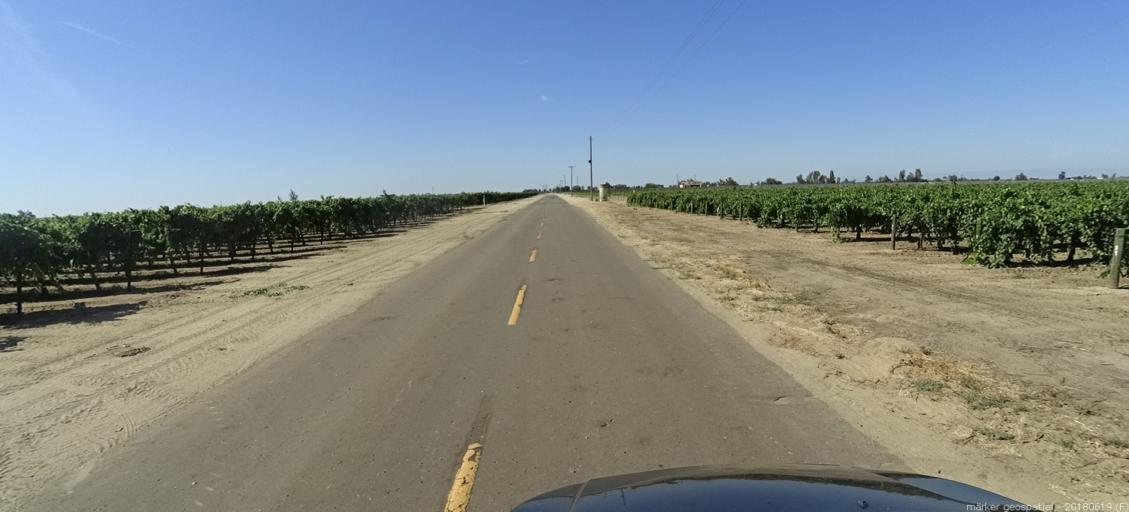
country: US
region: California
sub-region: Fresno County
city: Biola
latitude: 36.8268
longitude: -120.0428
